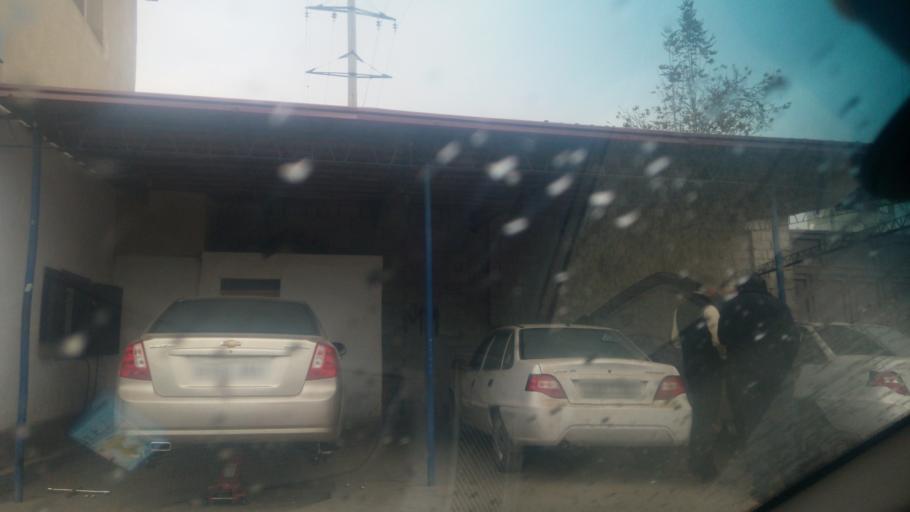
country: UZ
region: Sirdaryo
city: Guliston
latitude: 40.5140
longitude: 68.7654
